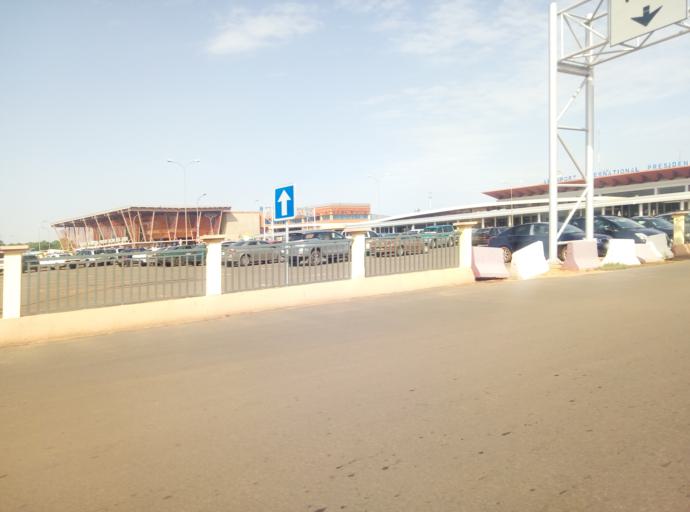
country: ML
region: Bamako
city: Bamako
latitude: 12.5415
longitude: -7.9486
